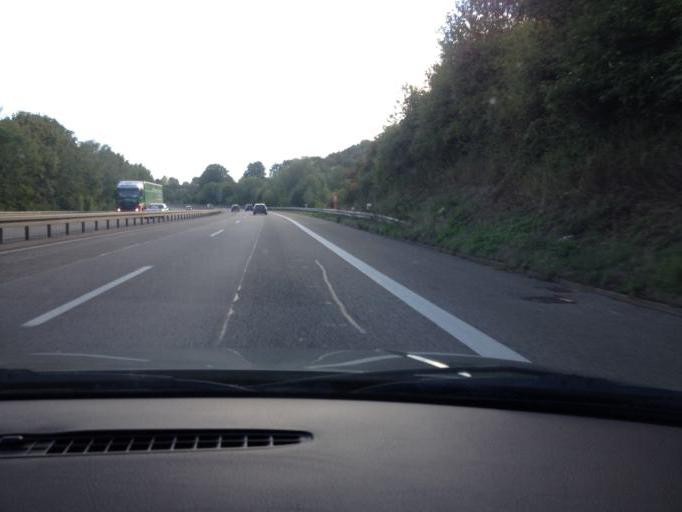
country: DE
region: Saarland
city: Eppelborn
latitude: 49.4035
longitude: 7.0104
